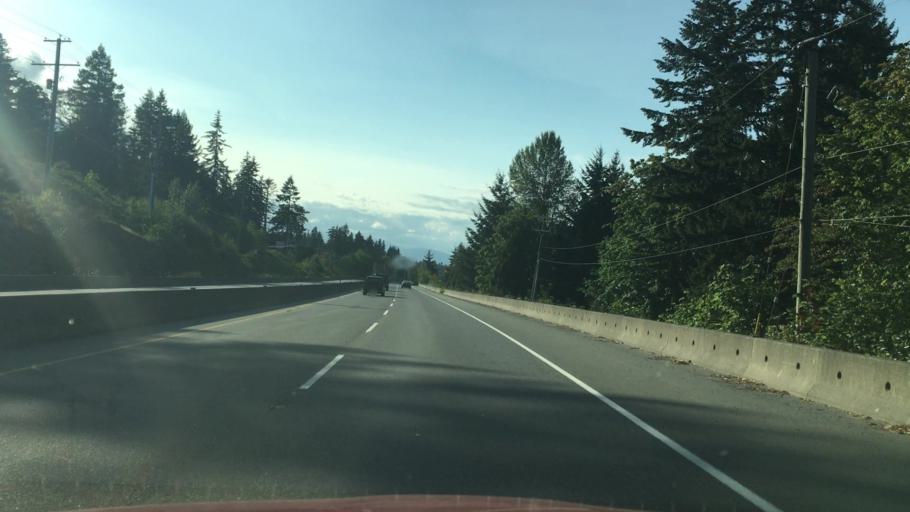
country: CA
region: British Columbia
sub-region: Cowichan Valley Regional District
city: Ladysmith
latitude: 48.9646
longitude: -123.7839
